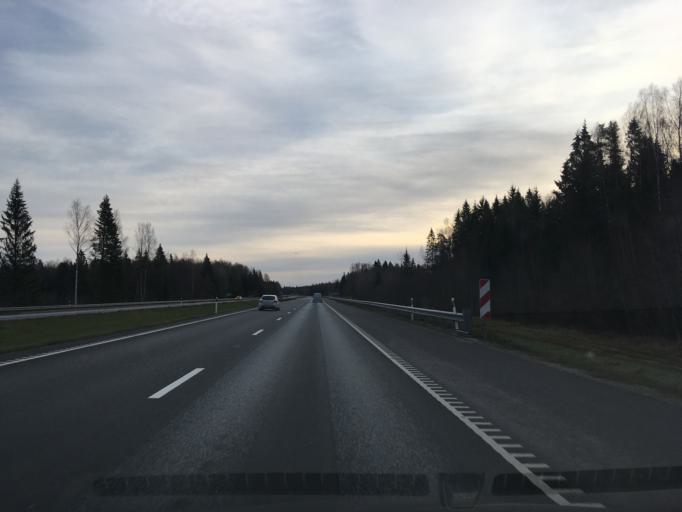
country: EE
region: Harju
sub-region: Loksa linn
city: Loksa
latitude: 59.4621
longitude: 25.7668
